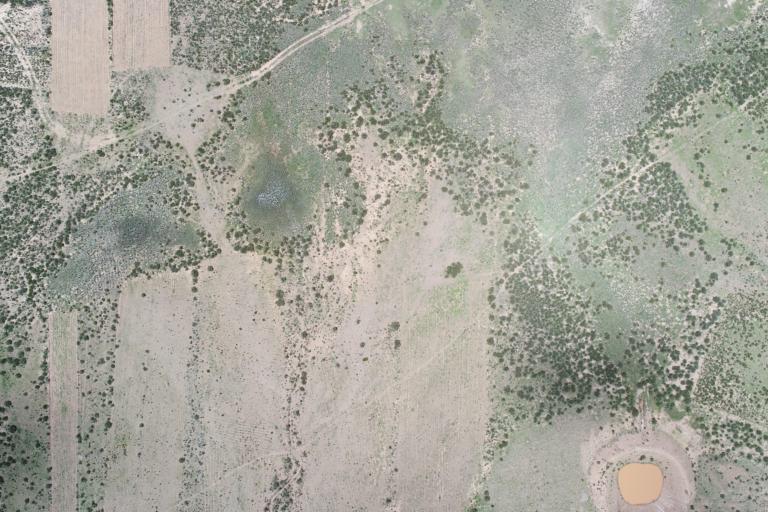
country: BO
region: La Paz
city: Curahuara de Carangas
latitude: -17.3213
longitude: -68.5118
